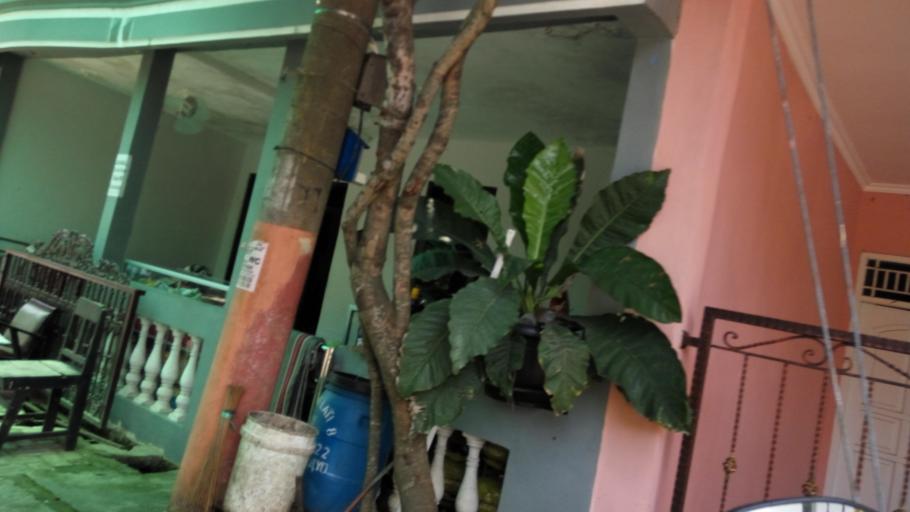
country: ID
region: Central Java
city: Mranggen
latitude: -7.0429
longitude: 110.4764
